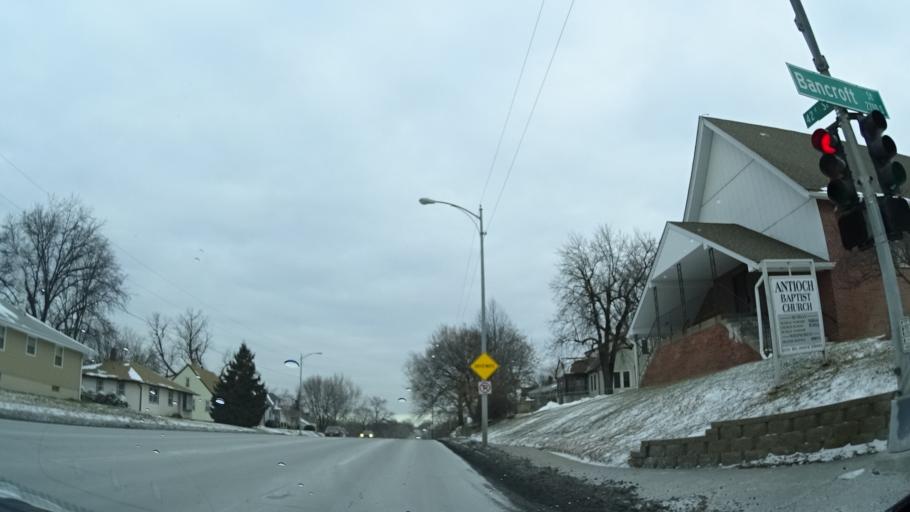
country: US
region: Nebraska
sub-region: Douglas County
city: Omaha
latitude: 41.2342
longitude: -95.9758
